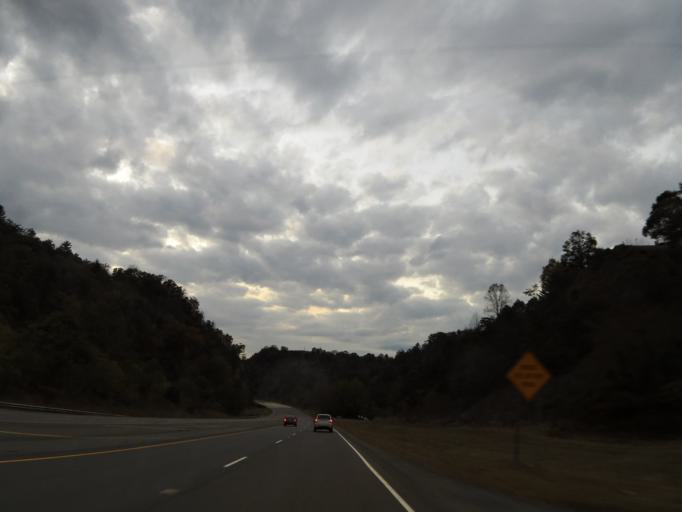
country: US
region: North Carolina
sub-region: Madison County
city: Marshall
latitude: 35.7659
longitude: -82.6140
